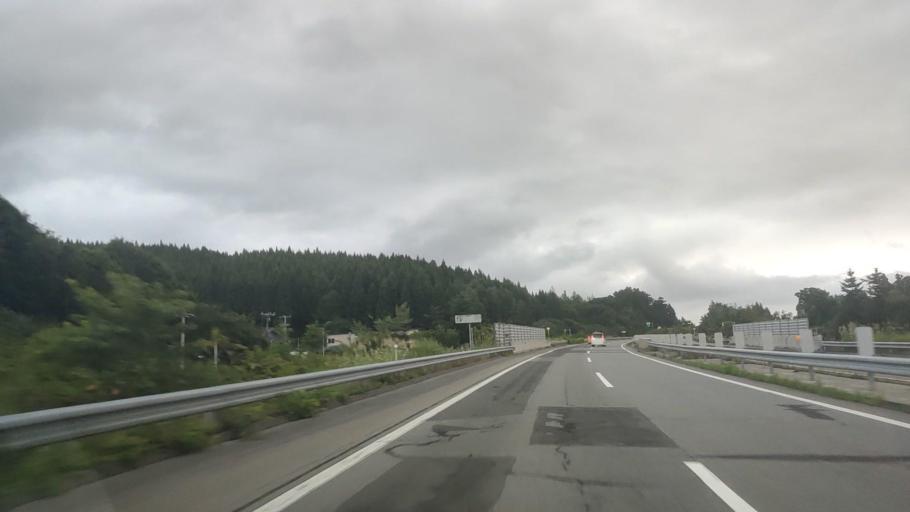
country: JP
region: Hokkaido
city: Nanae
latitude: 41.8993
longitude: 140.7054
